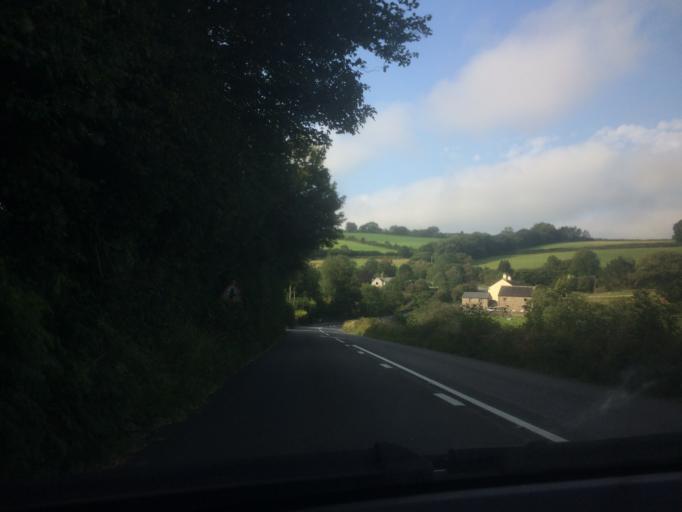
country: GB
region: England
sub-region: Devon
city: Tavistock
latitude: 50.5384
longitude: -4.1739
